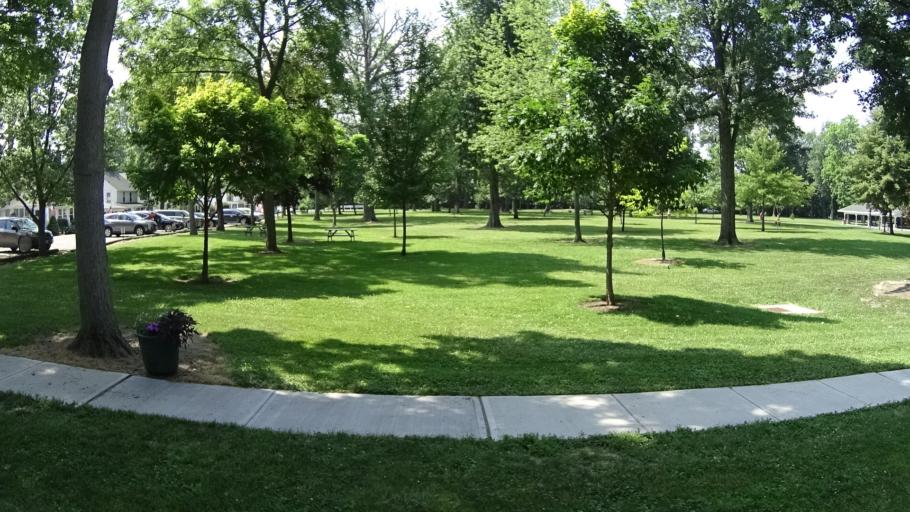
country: US
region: Ohio
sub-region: Lorain County
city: Vermilion
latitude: 41.4261
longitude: -82.3551
